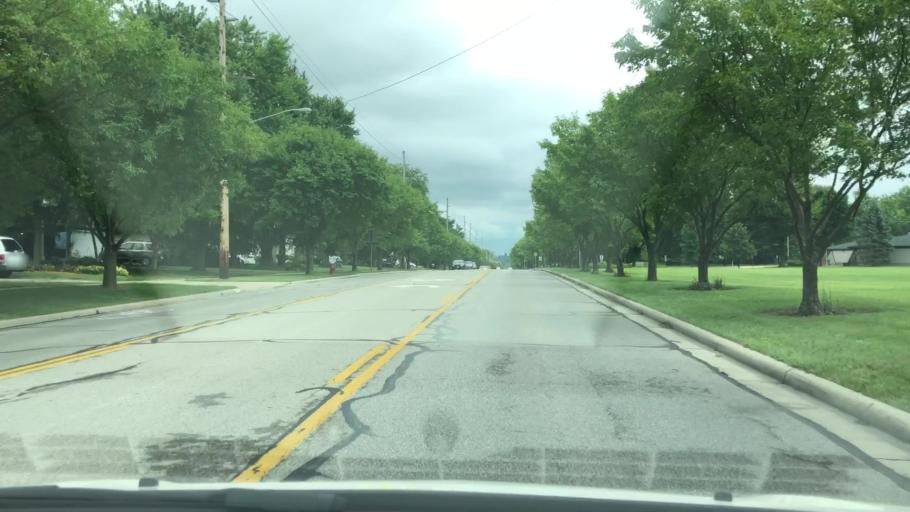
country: US
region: Ohio
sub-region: Franklin County
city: Westerville
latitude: 40.1253
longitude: -82.9633
